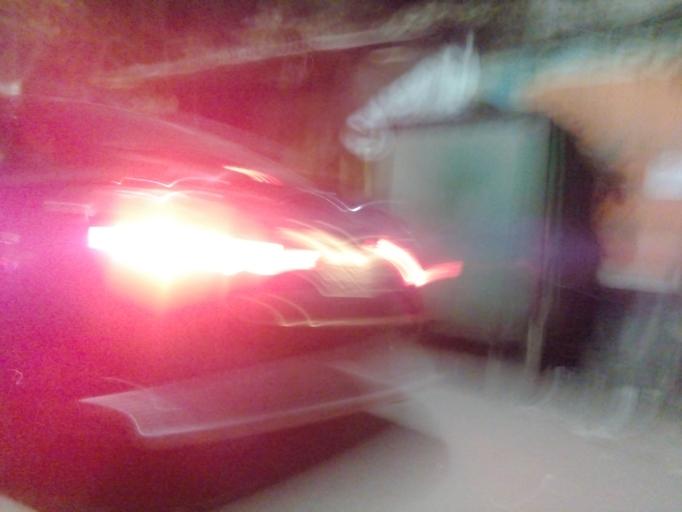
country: BD
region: Dhaka
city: Paltan
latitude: 23.7498
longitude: 90.4257
